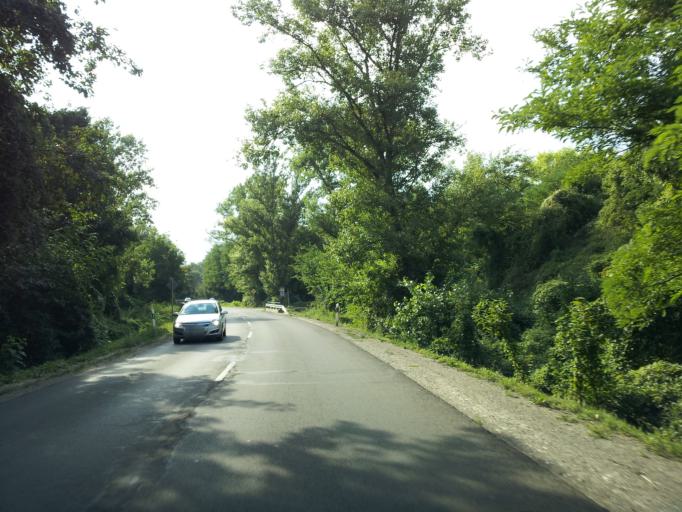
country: HU
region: Pest
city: Dunabogdany
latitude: 47.8136
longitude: 19.0797
